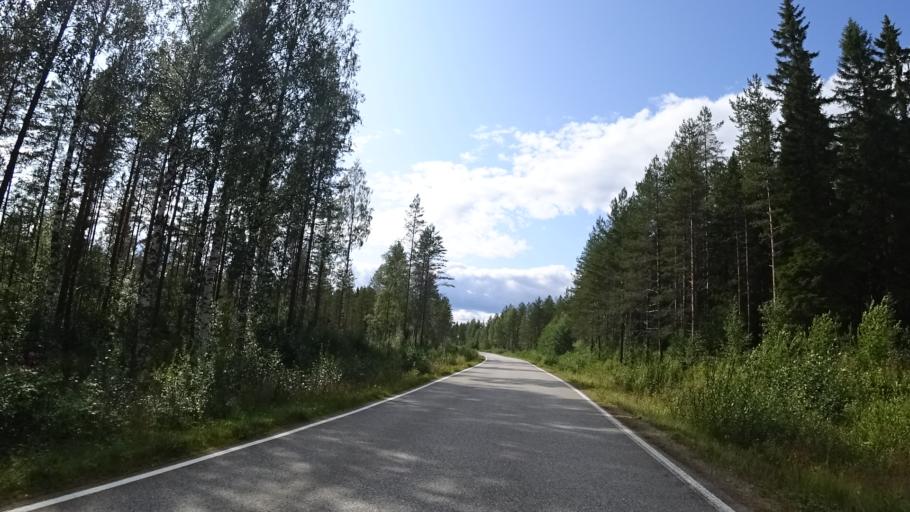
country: FI
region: North Karelia
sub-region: Joensuu
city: Ilomantsi
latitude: 62.4127
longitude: 30.9870
